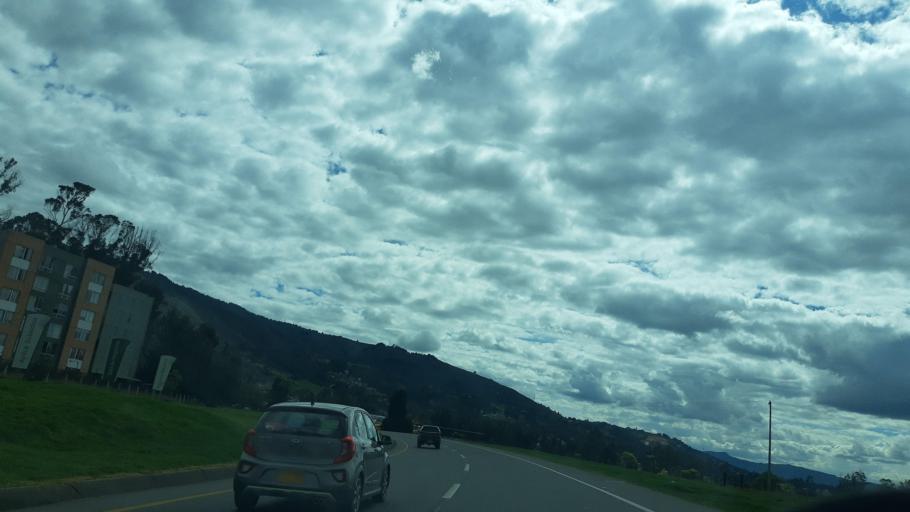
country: CO
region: Cundinamarca
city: Gachancipa
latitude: 4.9893
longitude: -73.8800
